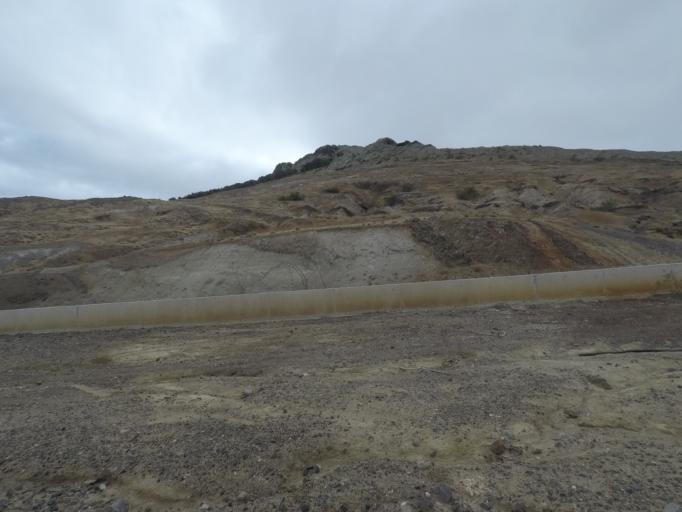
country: PT
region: Madeira
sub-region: Porto Santo
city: Vila de Porto Santo
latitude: 33.0480
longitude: -16.3654
